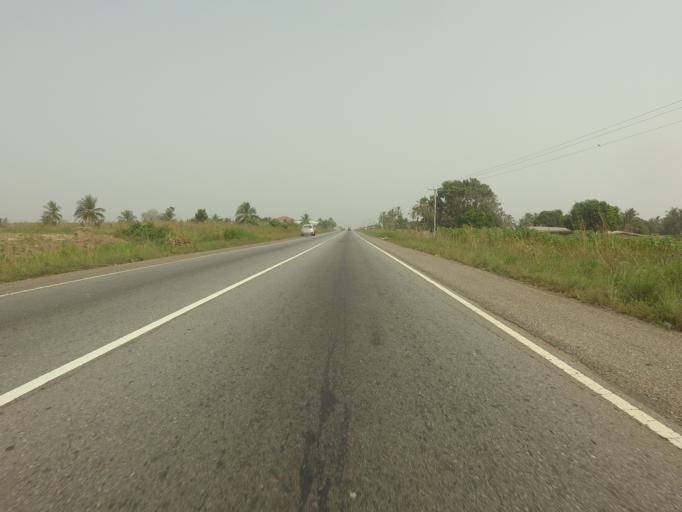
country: GH
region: Volta
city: Anloga
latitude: 5.8915
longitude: 0.4838
